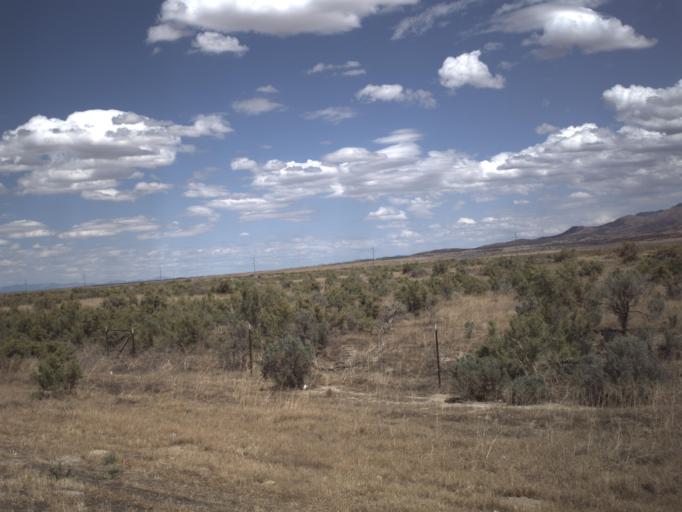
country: US
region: Utah
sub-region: Millard County
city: Delta
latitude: 39.2325
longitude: -112.4281
